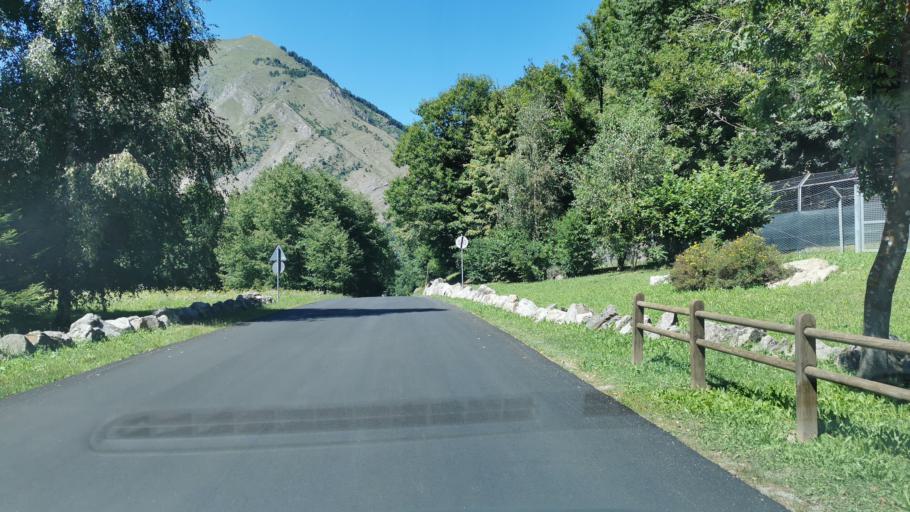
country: IT
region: Piedmont
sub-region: Provincia di Cuneo
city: Entracque
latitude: 44.2507
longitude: 7.3842
